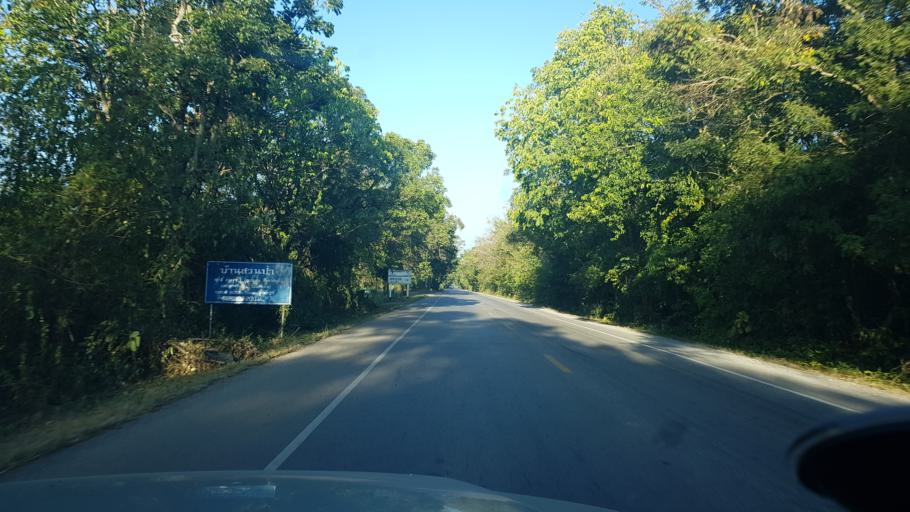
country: TH
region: Khon Kaen
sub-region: Amphoe Phu Pha Man
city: Phu Pha Man
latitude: 16.6244
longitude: 101.8559
